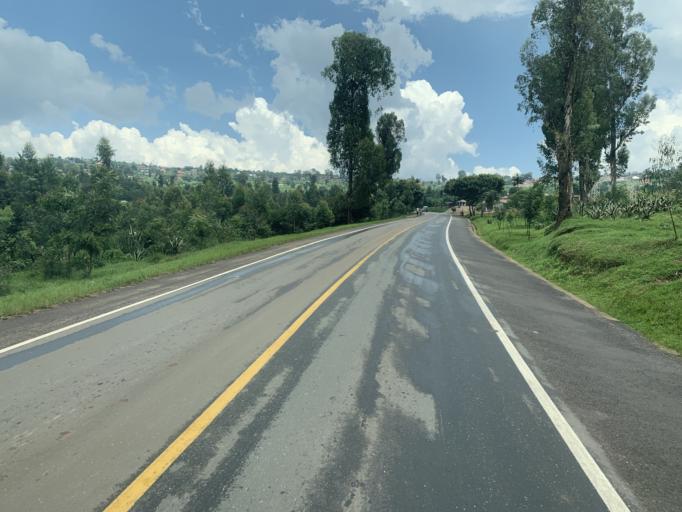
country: RW
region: Southern Province
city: Gitarama
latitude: -2.0066
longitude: 29.8962
